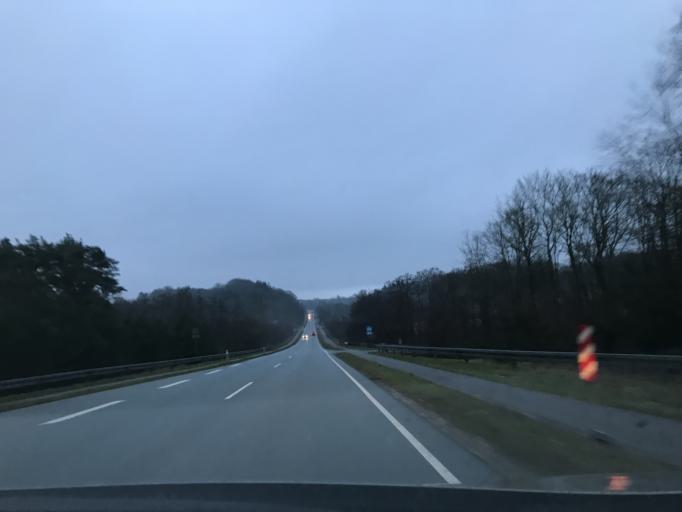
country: DK
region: Central Jutland
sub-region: Hedensted Kommune
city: Hedensted
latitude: 55.7154
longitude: 9.7357
